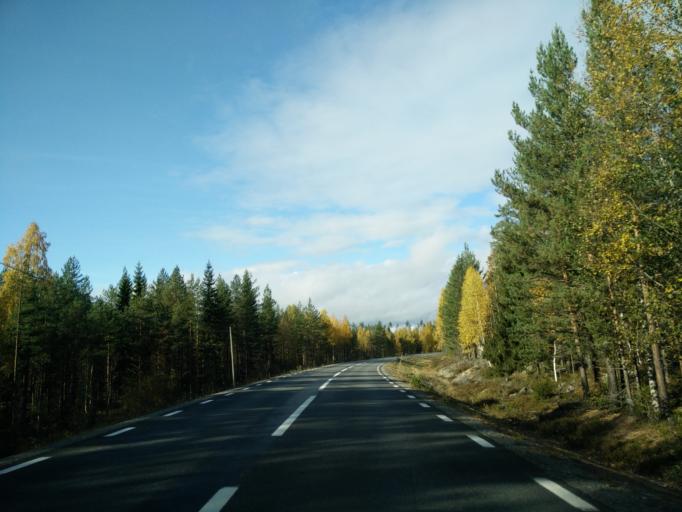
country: SE
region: Jaemtland
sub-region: Braecke Kommun
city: Braecke
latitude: 62.3883
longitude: 15.1105
